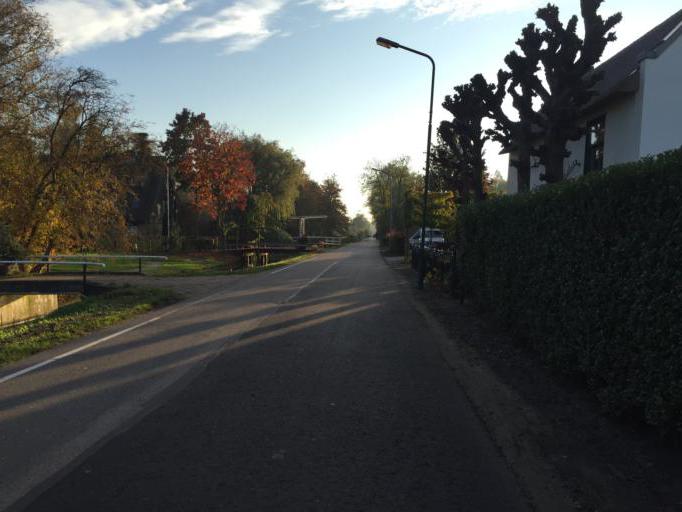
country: NL
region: North Holland
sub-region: Gemeente Wijdemeren
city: Kortenhoef
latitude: 52.2742
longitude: 5.1069
